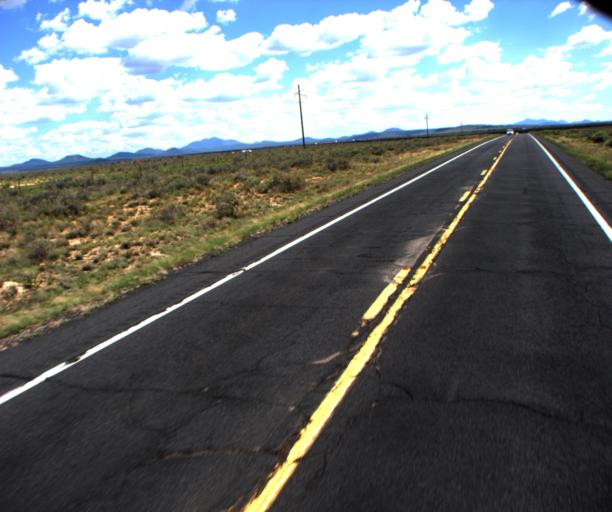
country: US
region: Arizona
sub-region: Coconino County
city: Williams
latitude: 35.6264
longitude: -112.1430
